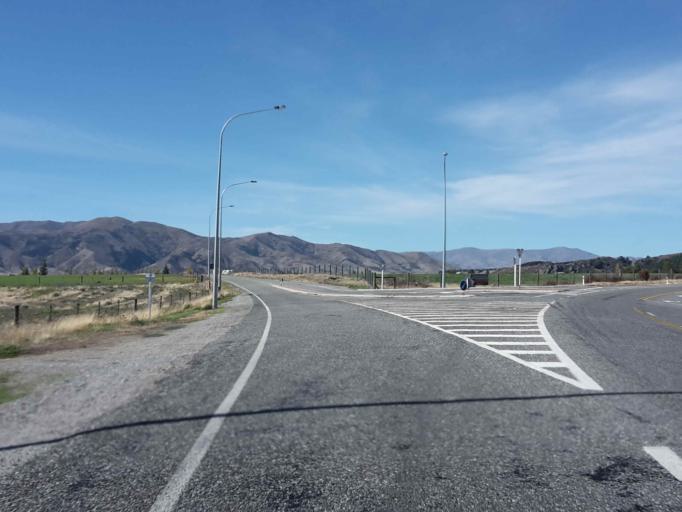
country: NZ
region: Otago
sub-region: Queenstown-Lakes District
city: Wanaka
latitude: -44.7335
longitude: 169.2583
